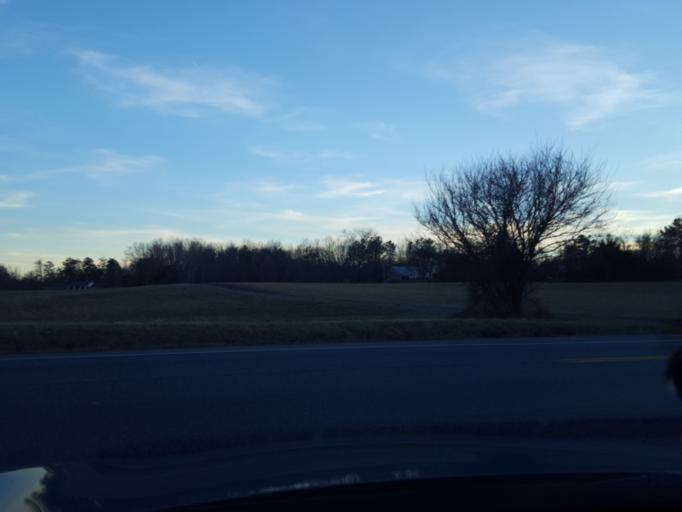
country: US
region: Maryland
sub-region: Saint Mary's County
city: Golden Beach
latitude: 38.5147
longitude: -76.6972
